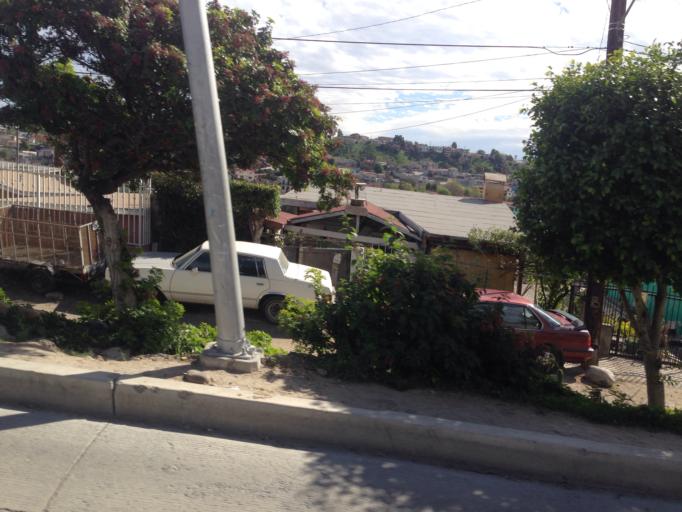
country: MX
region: Baja California
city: Tijuana
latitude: 32.5357
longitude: -116.9955
